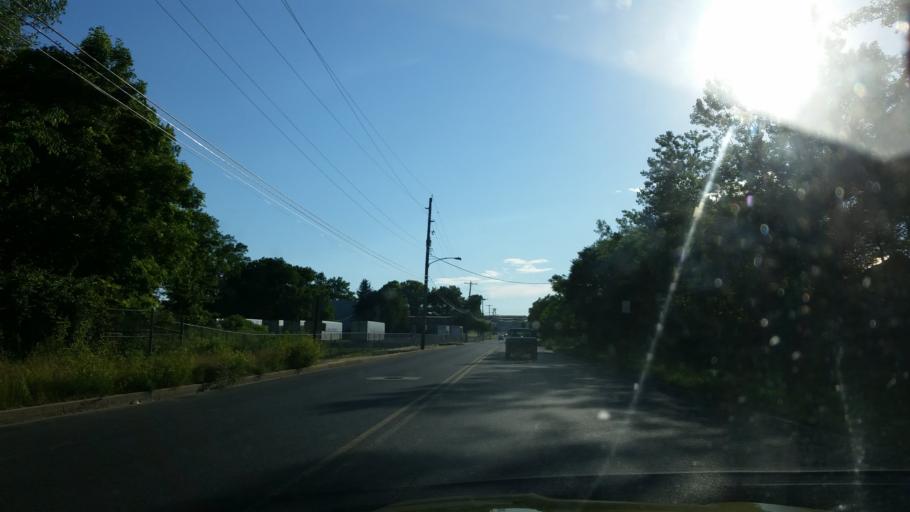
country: US
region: Pennsylvania
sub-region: Lebanon County
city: Pleasant Hill
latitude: 40.3449
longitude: -76.4370
